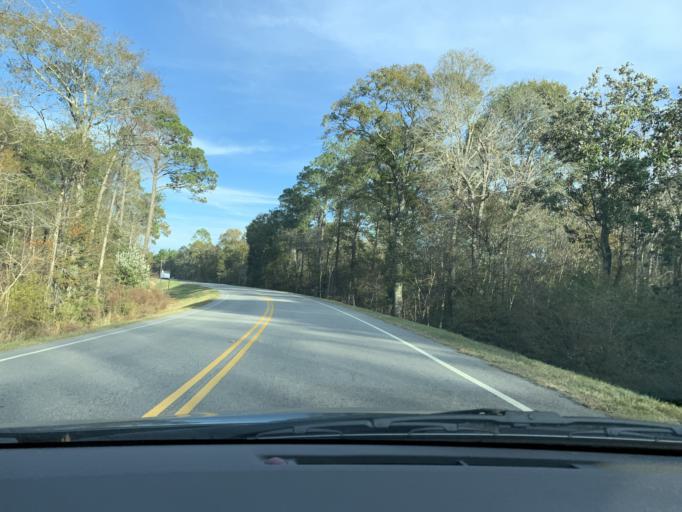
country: US
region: Georgia
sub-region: Tift County
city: Tifton
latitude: 31.6087
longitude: -83.4468
